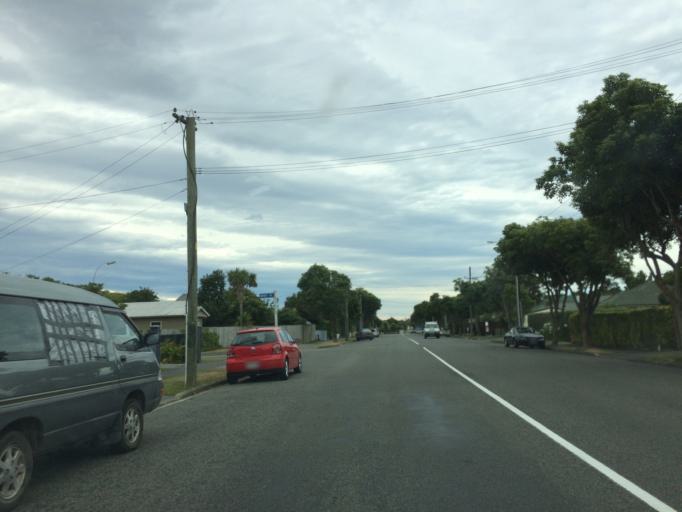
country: NZ
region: Canterbury
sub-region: Selwyn District
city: Prebbleton
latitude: -43.5193
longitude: 172.5443
